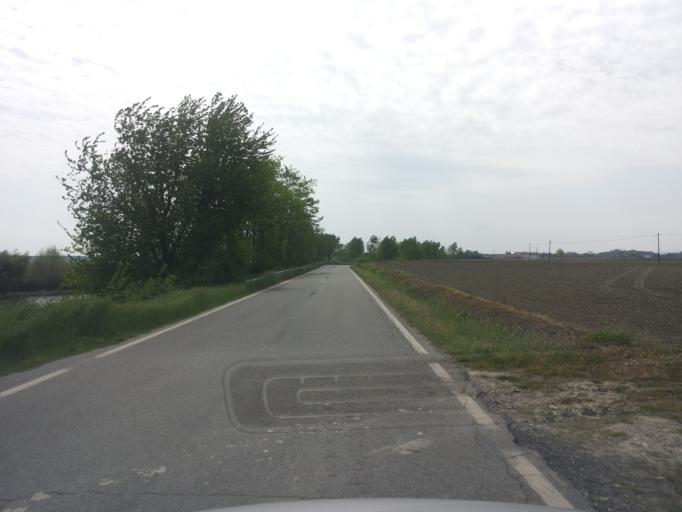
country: IT
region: Piedmont
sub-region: Provincia di Vercelli
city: Motta De Conti
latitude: 45.2060
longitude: 8.5149
